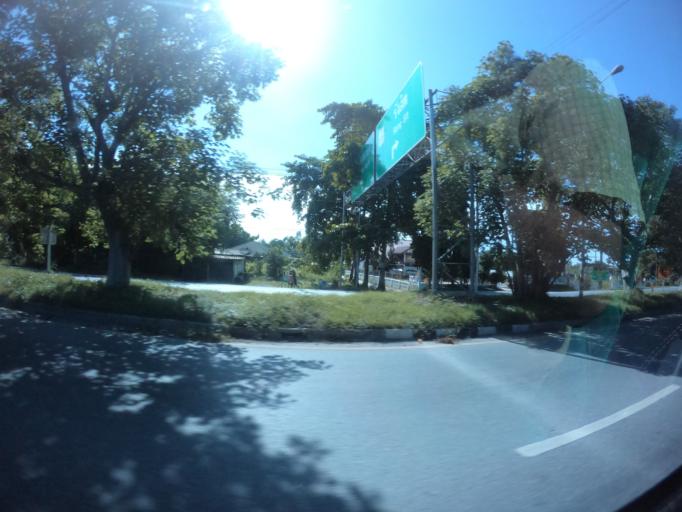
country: TH
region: Nakhon Nayok
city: Ban Na
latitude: 14.2088
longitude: 101.0687
